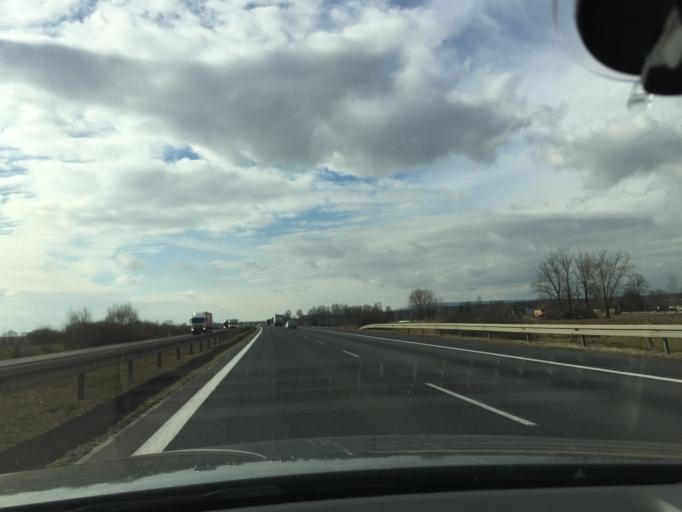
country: PL
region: Lodz Voivodeship
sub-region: Powiat piotrkowski
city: Wola Krzysztoporska
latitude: 51.2862
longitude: 19.5387
